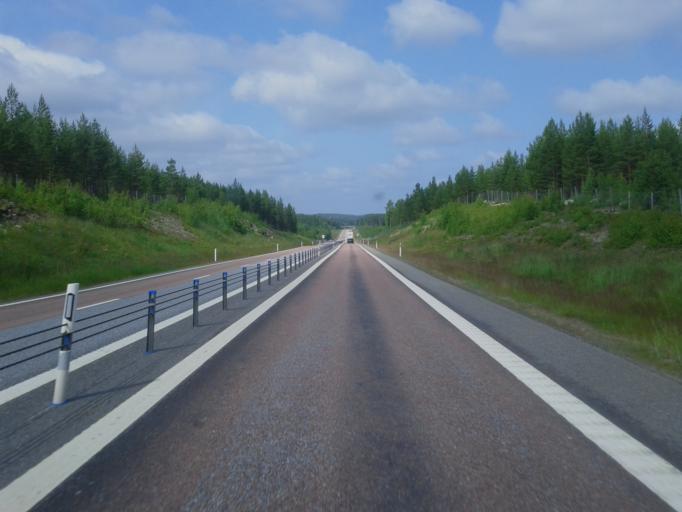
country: SE
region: Vaesterbotten
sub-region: Skelleftea Kommun
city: Soedra Bergsbyn
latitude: 64.6902
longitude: 21.0412
